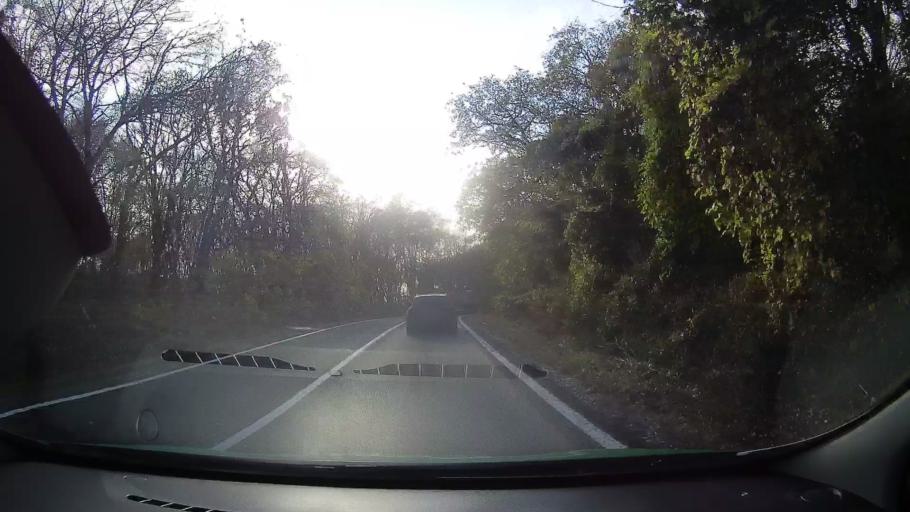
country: RO
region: Tulcea
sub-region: Comuna Topolog
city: Topolog
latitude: 44.9074
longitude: 28.4177
